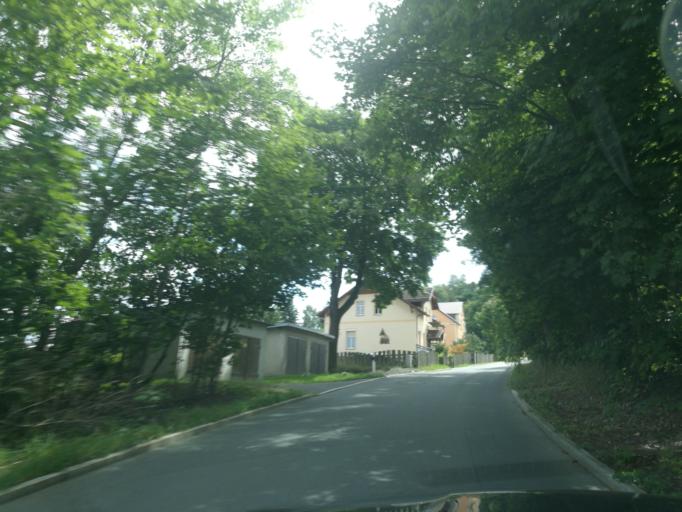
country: DE
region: Saxony
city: Adorf
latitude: 50.3138
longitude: 12.2665
